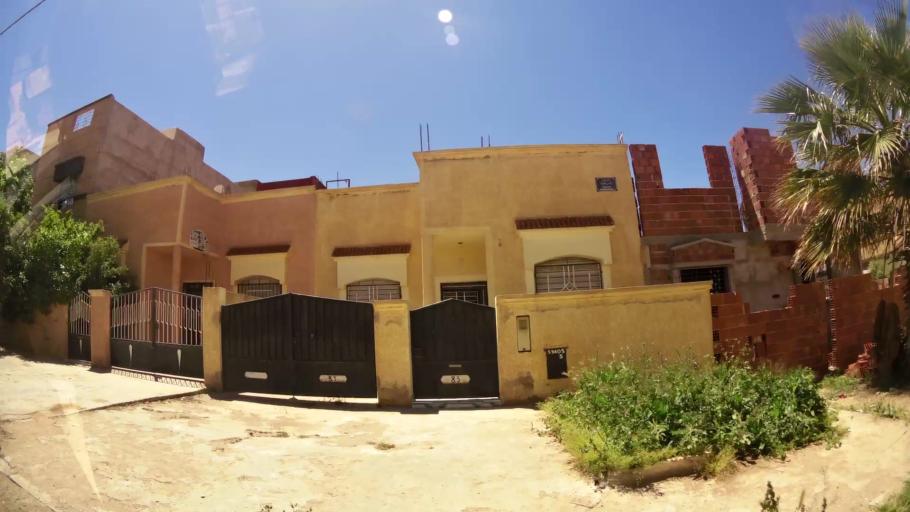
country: MA
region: Oriental
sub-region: Oujda-Angad
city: Oujda
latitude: 34.6778
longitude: -1.8562
